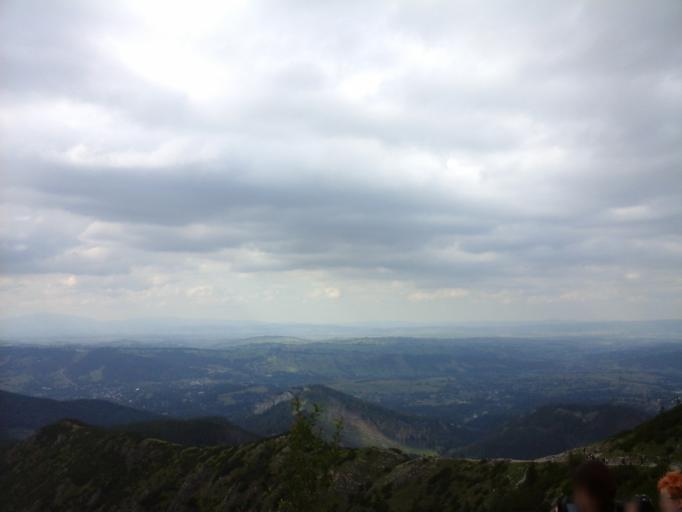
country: PL
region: Lesser Poland Voivodeship
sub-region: Powiat tatrzanski
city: Zakopane
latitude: 49.2551
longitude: 20.0035
